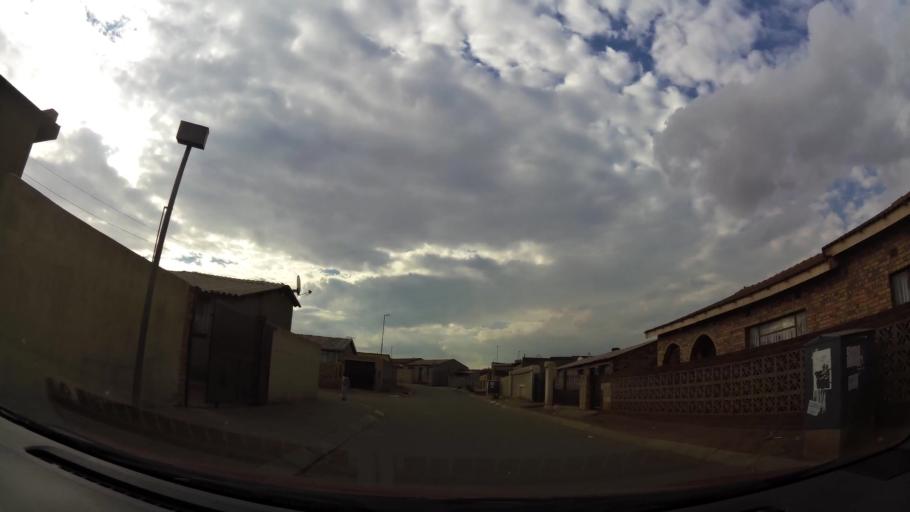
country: ZA
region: Gauteng
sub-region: City of Johannesburg Metropolitan Municipality
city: Soweto
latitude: -26.2473
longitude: 27.8365
